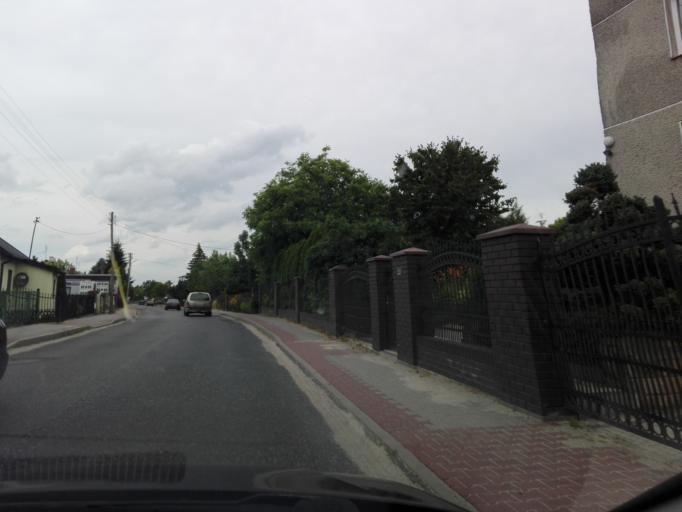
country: PL
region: Lublin Voivodeship
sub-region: Powiat pulawski
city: Kurow
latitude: 51.3911
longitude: 22.1899
